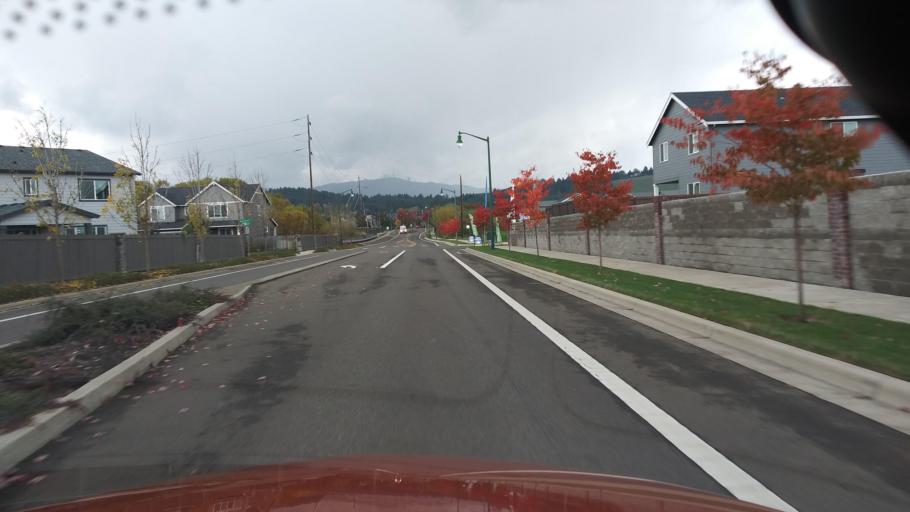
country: US
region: Oregon
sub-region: Washington County
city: Forest Grove
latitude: 45.5391
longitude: -123.1190
